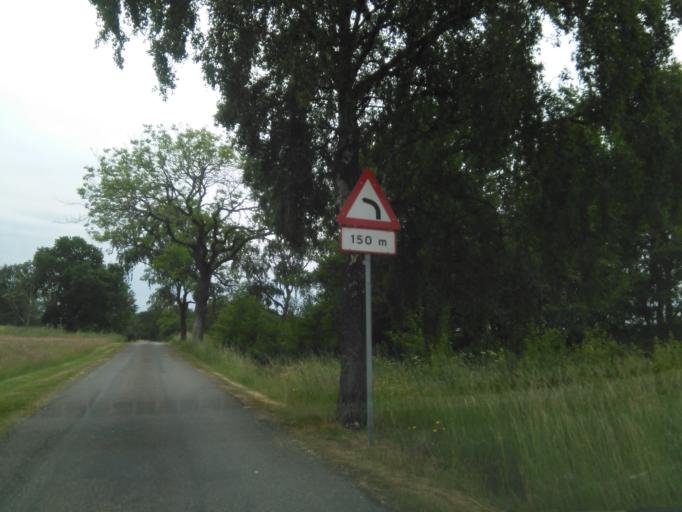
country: DK
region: Capital Region
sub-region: Bornholm Kommune
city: Akirkeby
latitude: 55.0938
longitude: 14.8831
